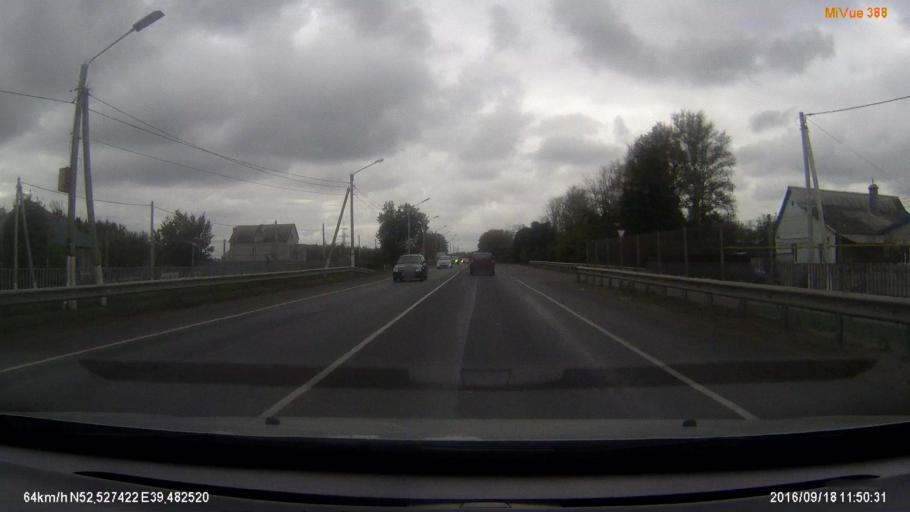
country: RU
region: Lipetsk
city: Syrskoye
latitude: 52.5276
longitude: 39.4828
